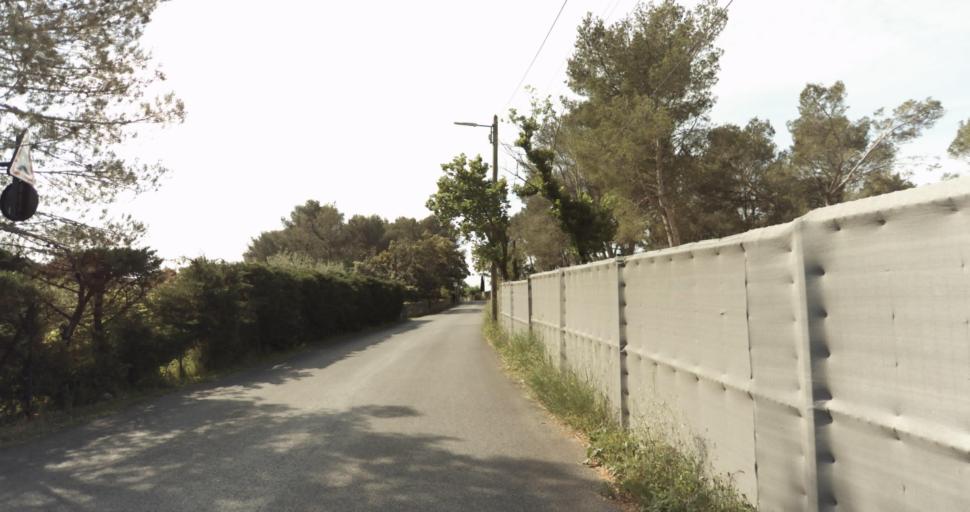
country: FR
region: Languedoc-Roussillon
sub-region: Departement du Gard
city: Poulx
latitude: 43.8713
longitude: 4.3938
